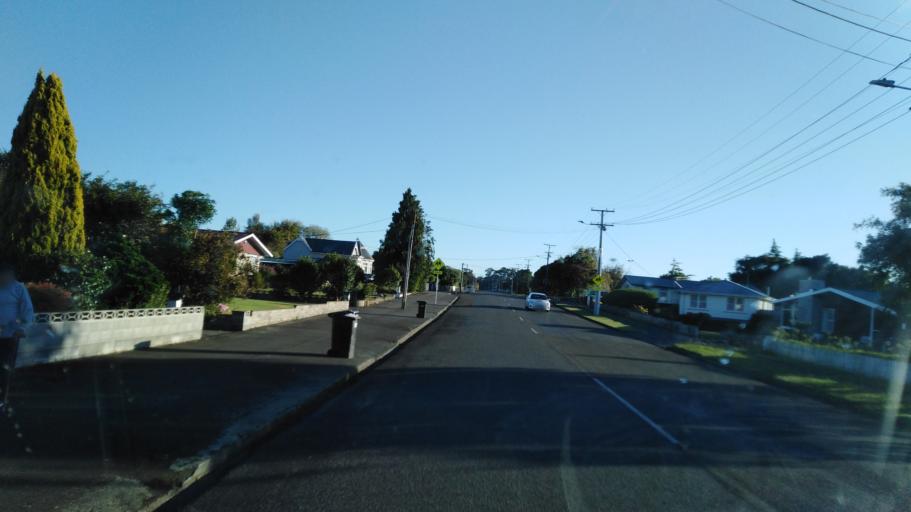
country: NZ
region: Manawatu-Wanganui
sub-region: Rangitikei District
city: Bulls
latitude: -40.0701
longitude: 175.3825
